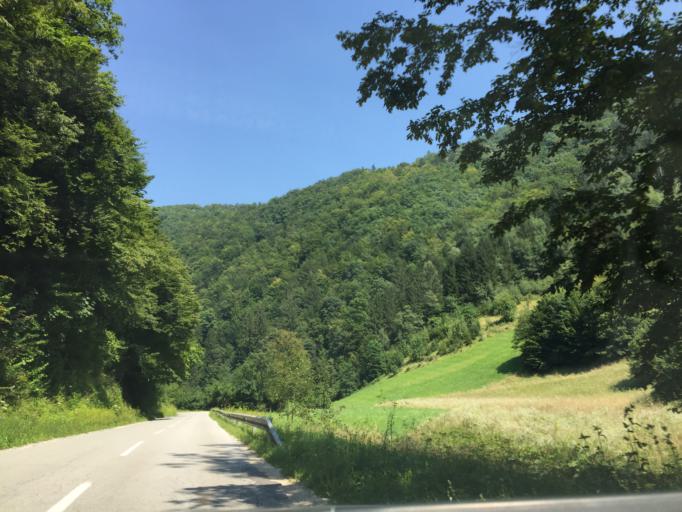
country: SI
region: Prebold
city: Prebold
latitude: 46.2140
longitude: 15.1000
